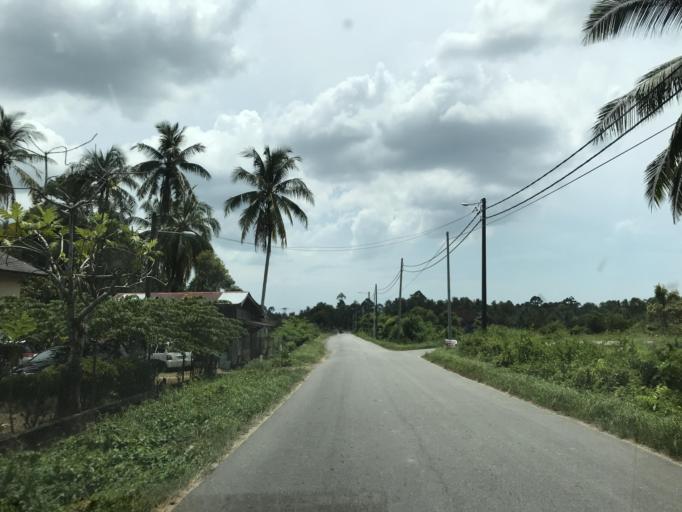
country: MY
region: Kelantan
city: Kota Bharu
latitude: 6.1471
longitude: 102.1874
